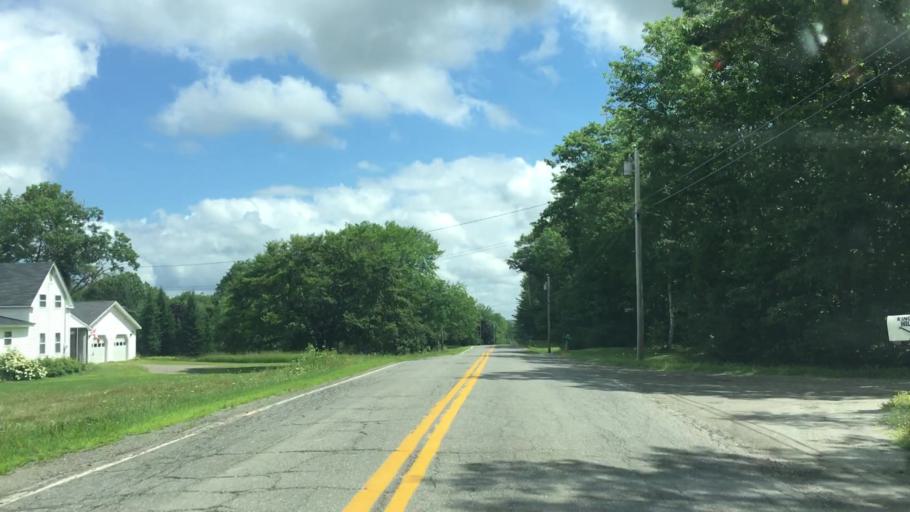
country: US
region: Maine
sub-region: Penobscot County
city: Carmel
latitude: 44.7942
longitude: -69.0720
